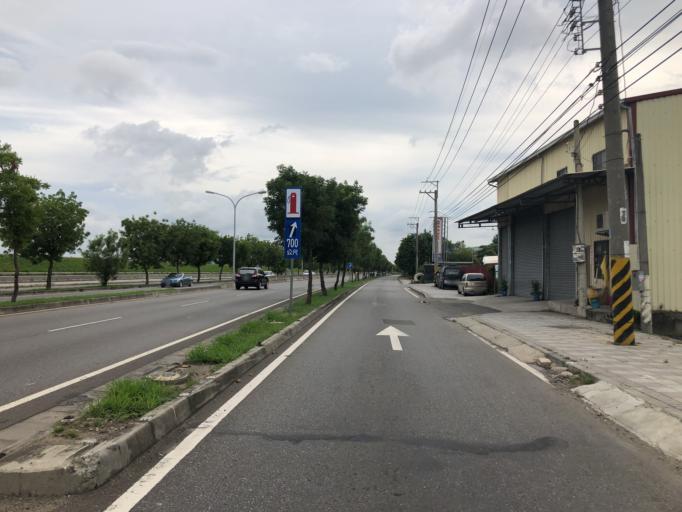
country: TW
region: Taiwan
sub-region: Taichung City
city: Taichung
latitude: 24.0840
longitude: 120.6710
